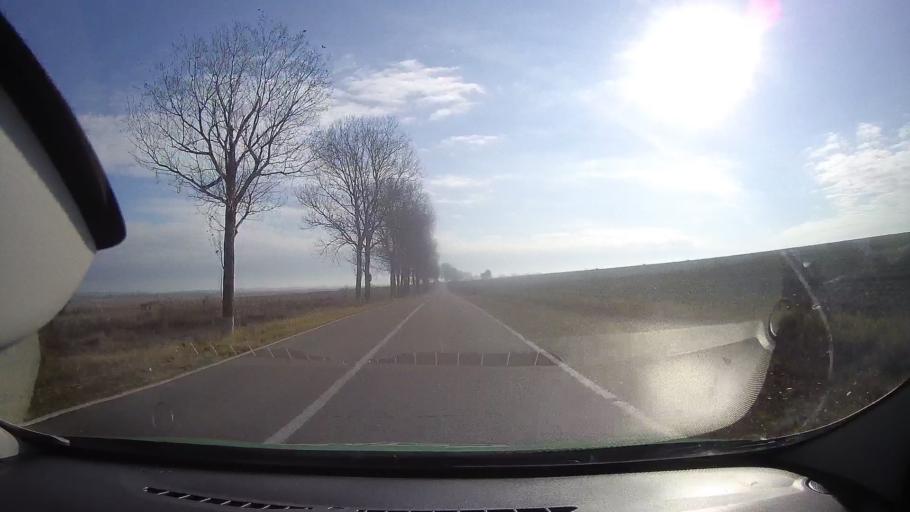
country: RO
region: Tulcea
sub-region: Comuna Mahmudia
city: Mahmudia
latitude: 45.0688
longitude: 29.1010
